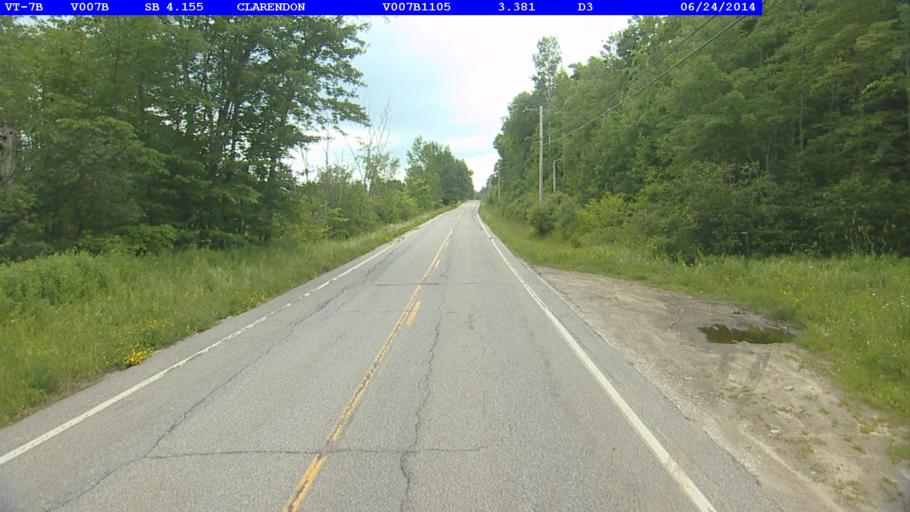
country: US
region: Vermont
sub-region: Rutland County
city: Rutland
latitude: 43.5473
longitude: -72.9574
